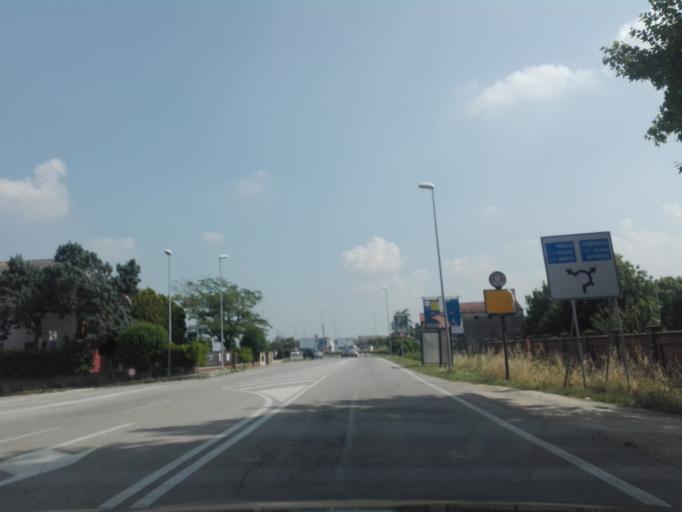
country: IT
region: Veneto
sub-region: Provincia di Rovigo
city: Adria
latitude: 45.0438
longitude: 12.0601
